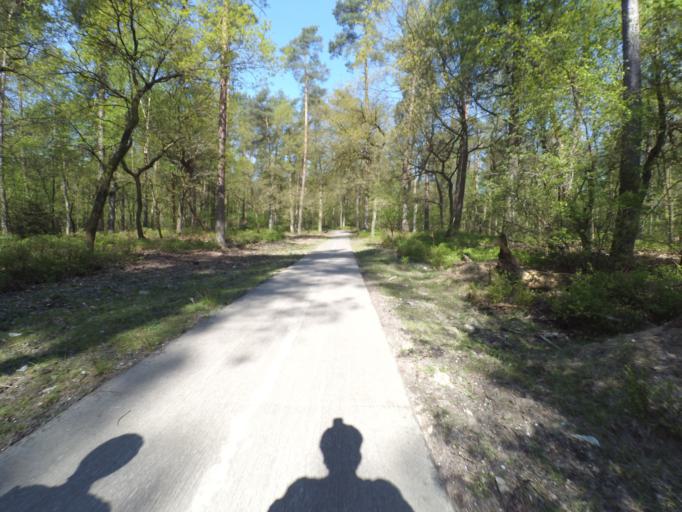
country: NL
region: Gelderland
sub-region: Gemeente Apeldoorn
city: Beekbergen
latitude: 52.1720
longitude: 5.9056
